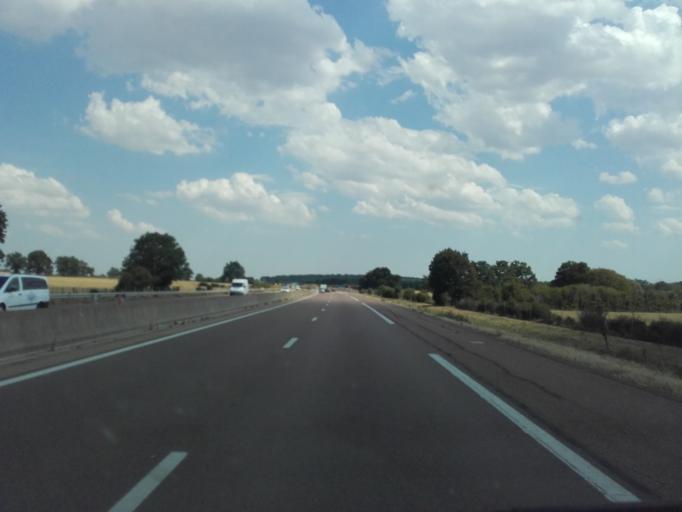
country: FR
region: Bourgogne
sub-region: Departement de l'Yonne
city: Avallon
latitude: 47.5073
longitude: 4.0074
